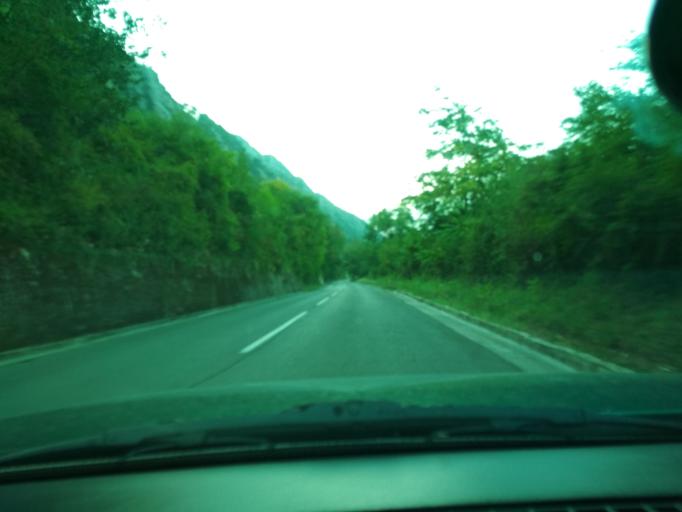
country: ME
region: Kotor
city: Kotor
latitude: 42.4144
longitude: 18.7612
